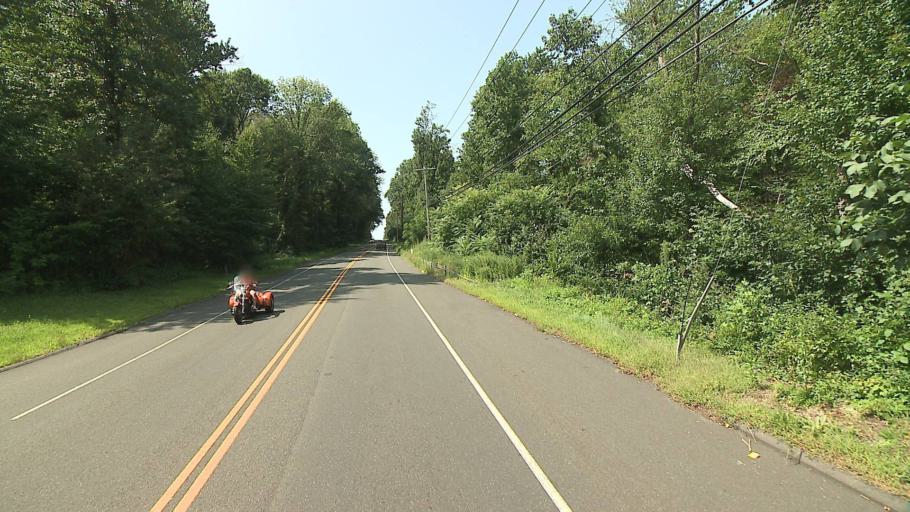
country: US
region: Connecticut
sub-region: Fairfield County
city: Shelton
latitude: 41.3323
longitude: -73.1416
